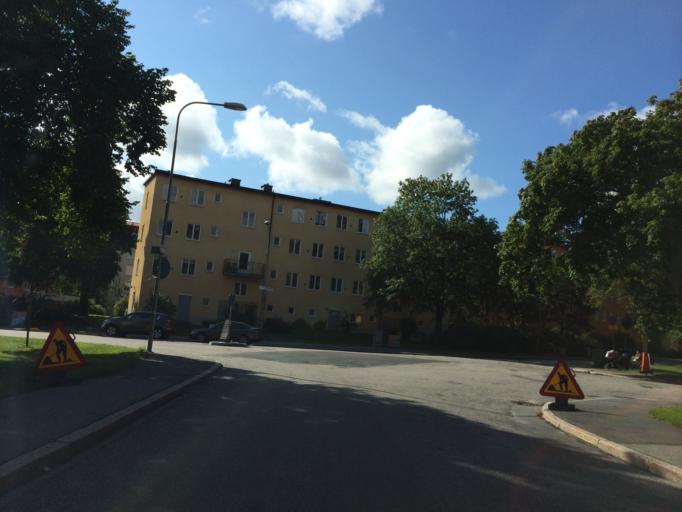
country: SE
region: Stockholm
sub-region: Stockholms Kommun
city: Arsta
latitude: 59.3013
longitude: 18.0024
